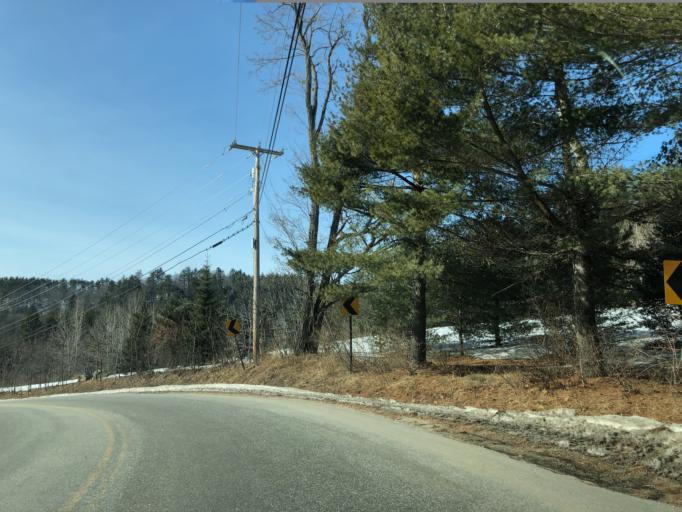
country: US
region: Maine
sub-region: Androscoggin County
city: Auburn
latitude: 44.1290
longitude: -70.2739
